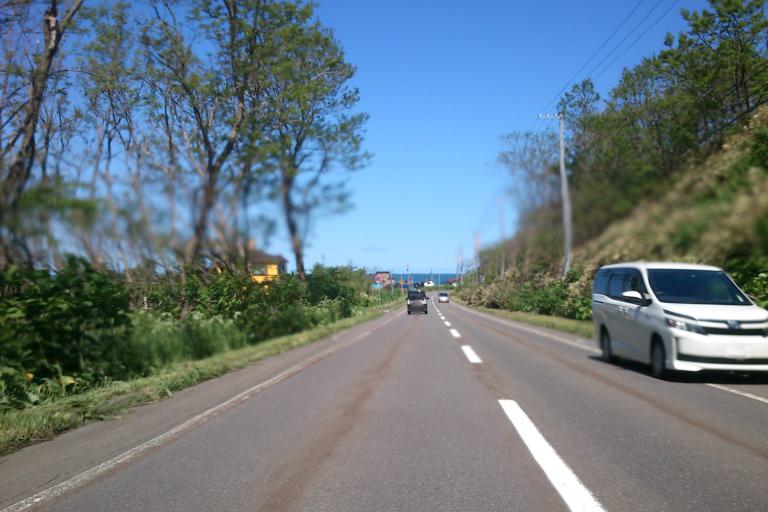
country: JP
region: Hokkaido
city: Ishikari
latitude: 43.5577
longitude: 141.3823
